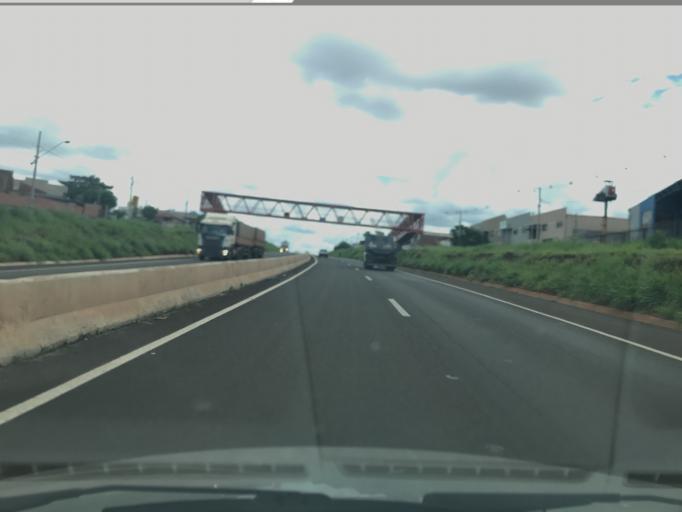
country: BR
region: Parana
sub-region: Maringa
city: Maringa
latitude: -23.3729
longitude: -51.9313
